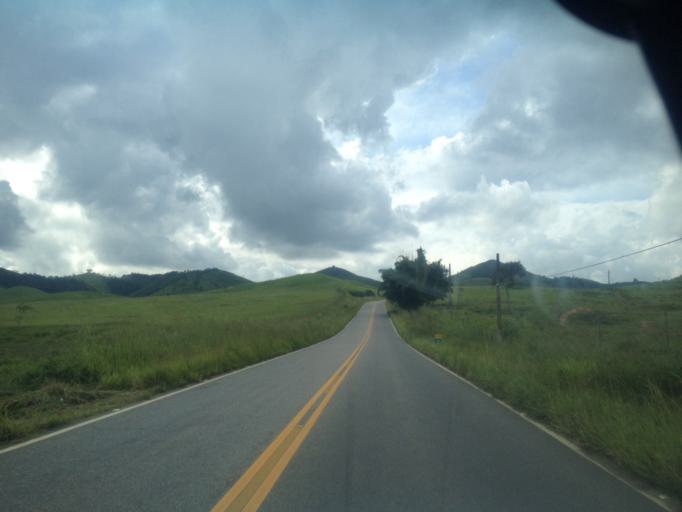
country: BR
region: Rio de Janeiro
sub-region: Quatis
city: Quatis
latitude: -22.3986
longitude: -44.2659
